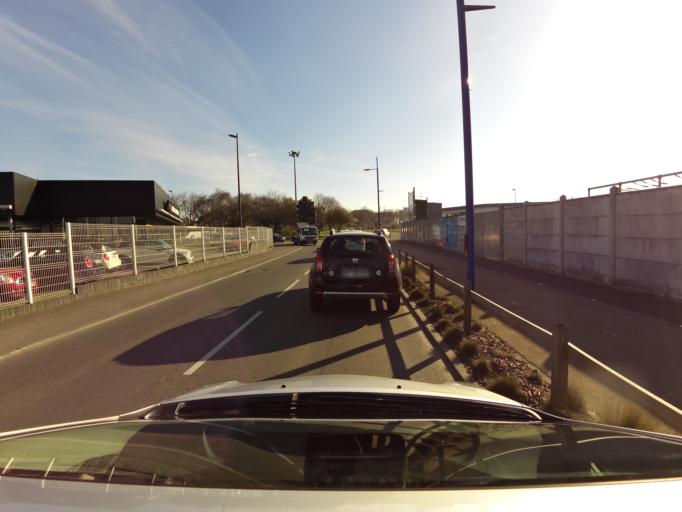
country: FR
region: Brittany
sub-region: Departement du Morbihan
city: Lorient
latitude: 47.7351
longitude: -3.3752
